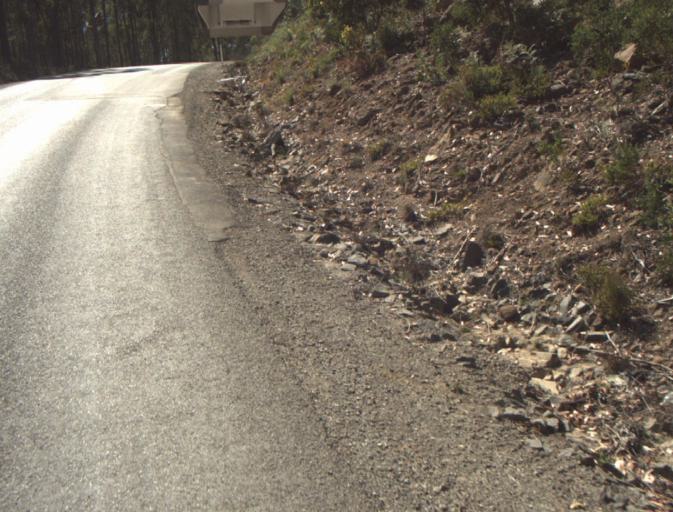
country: AU
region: Tasmania
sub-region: Launceston
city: Mayfield
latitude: -41.3359
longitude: 147.1984
